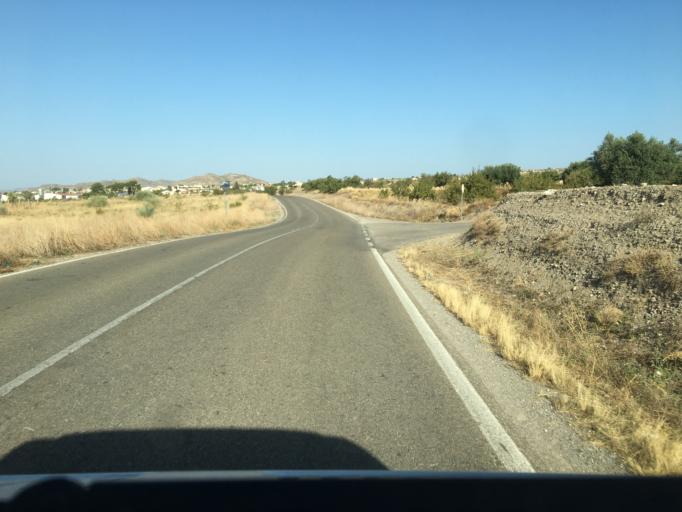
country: ES
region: Andalusia
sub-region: Provincia de Almeria
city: Huercal-Overa
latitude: 37.4700
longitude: -1.9055
